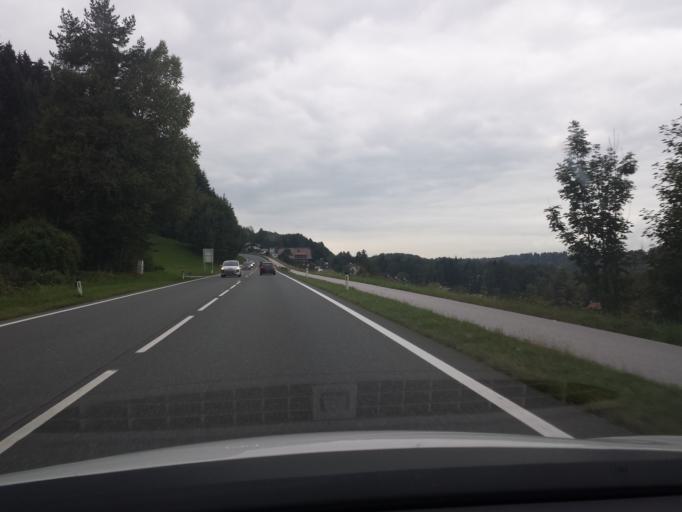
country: AT
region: Salzburg
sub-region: Politischer Bezirk Salzburg-Umgebung
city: Thalgau
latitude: 47.8120
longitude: 13.2441
